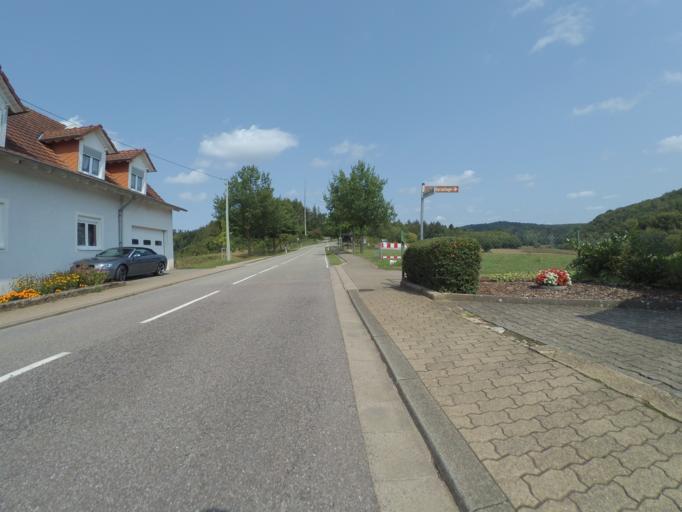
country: DE
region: Saarland
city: Britten
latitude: 49.5074
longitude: 6.6913
